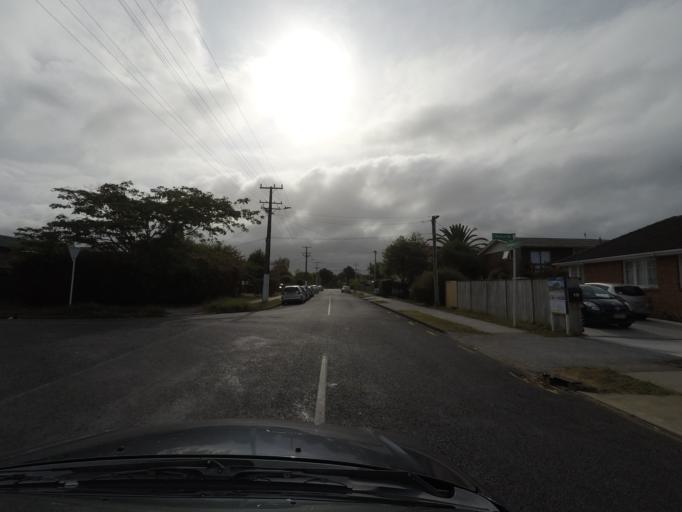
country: NZ
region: Auckland
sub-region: Auckland
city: Waitakere
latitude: -36.8981
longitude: 174.6694
